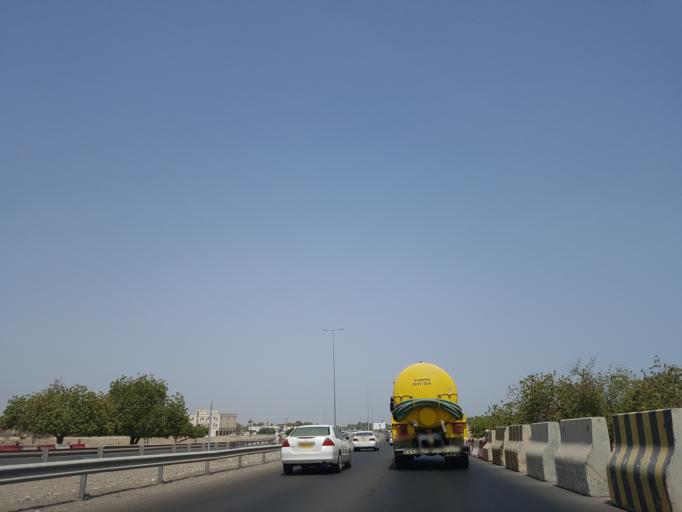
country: OM
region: Al Batinah
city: Saham
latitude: 24.1266
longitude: 56.8985
